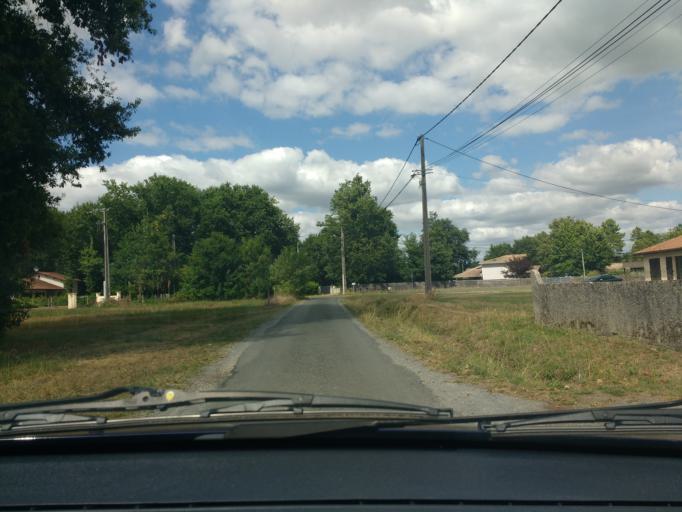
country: FR
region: Aquitaine
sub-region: Departement de la Gironde
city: Salles
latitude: 44.5644
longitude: -0.8414
